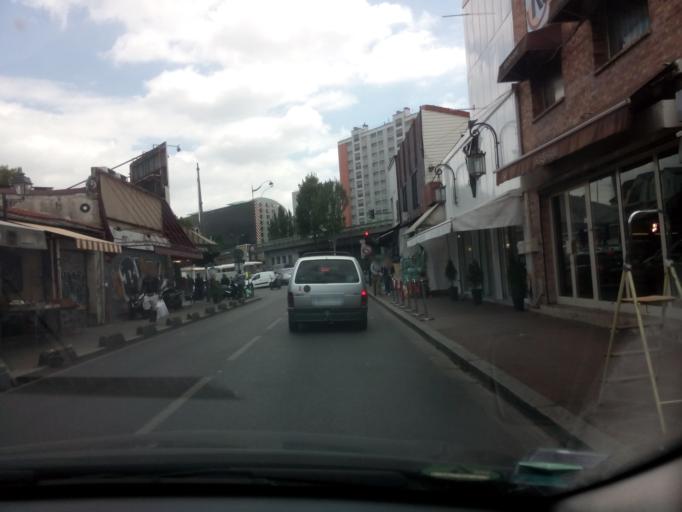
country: FR
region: Ile-de-France
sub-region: Paris
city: Saint-Ouen
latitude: 48.9017
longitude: 2.3434
